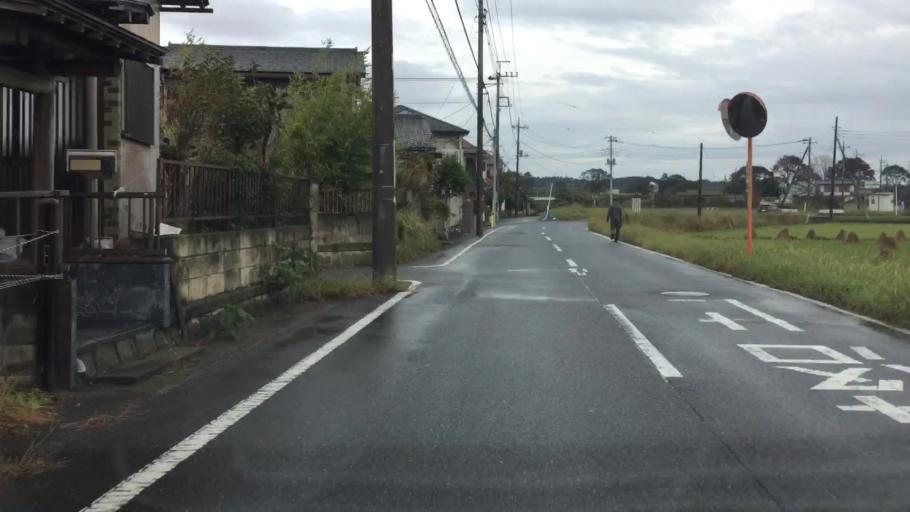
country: JP
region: Ibaraki
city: Toride
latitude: 35.8662
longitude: 140.1167
